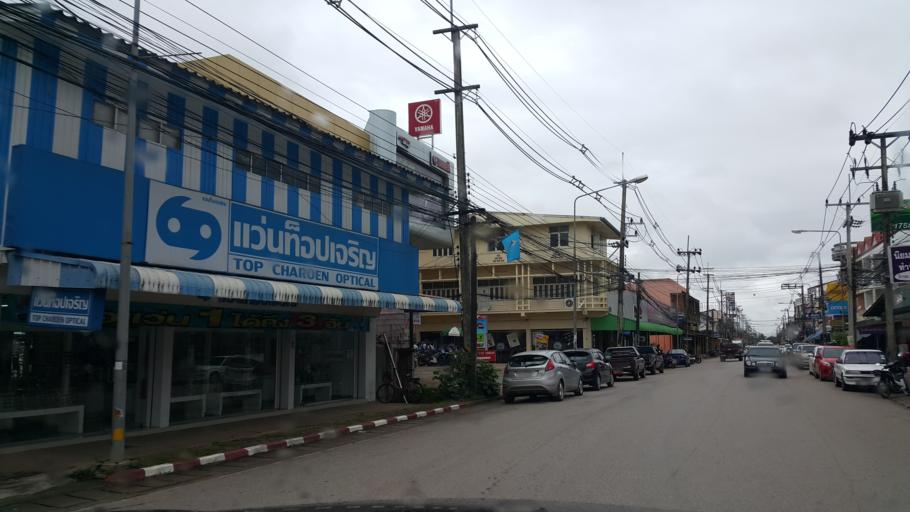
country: TH
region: Phayao
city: Chiang Kham
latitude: 19.5262
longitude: 100.3027
